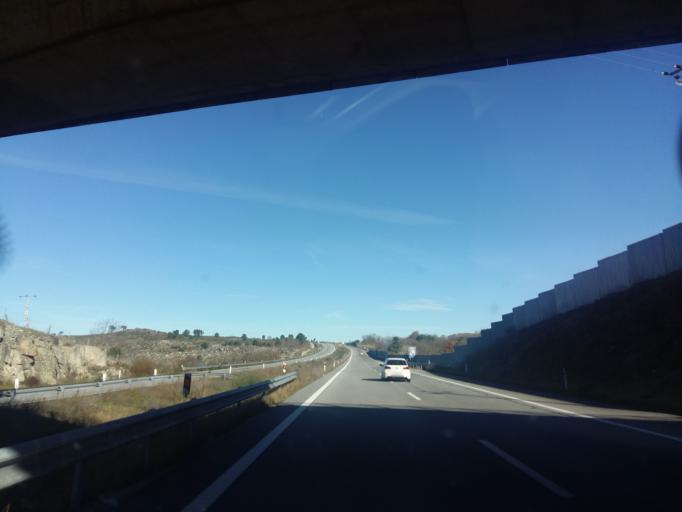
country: PT
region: Guarda
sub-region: Guarda
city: Sequeira
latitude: 40.5859
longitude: -7.1507
